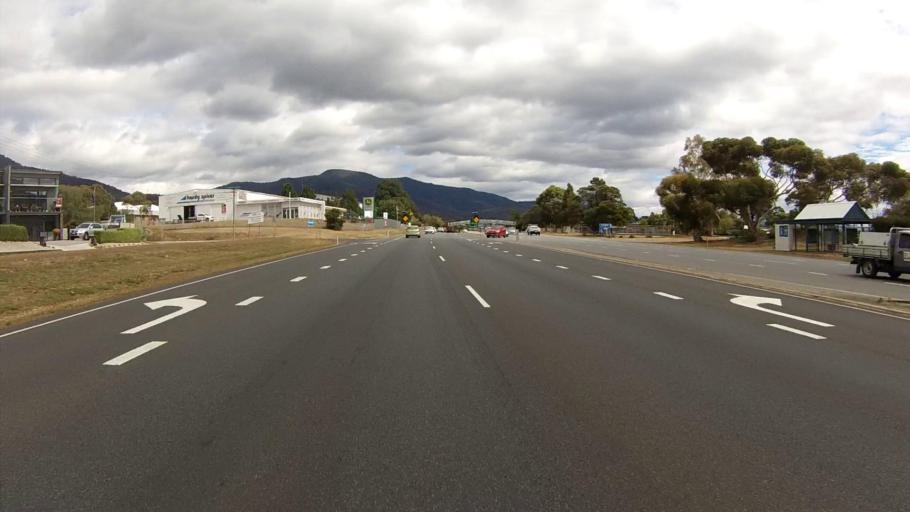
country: AU
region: Tasmania
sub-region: Glenorchy
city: Glenorchy
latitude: -42.8228
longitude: 147.2683
